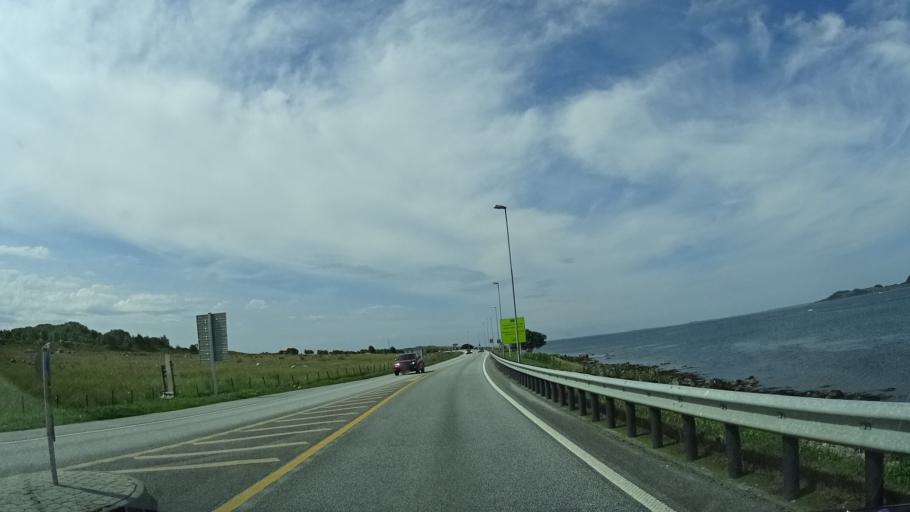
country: NO
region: Rogaland
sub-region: Rennesoy
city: Vikevag
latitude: 59.0566
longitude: 5.6672
